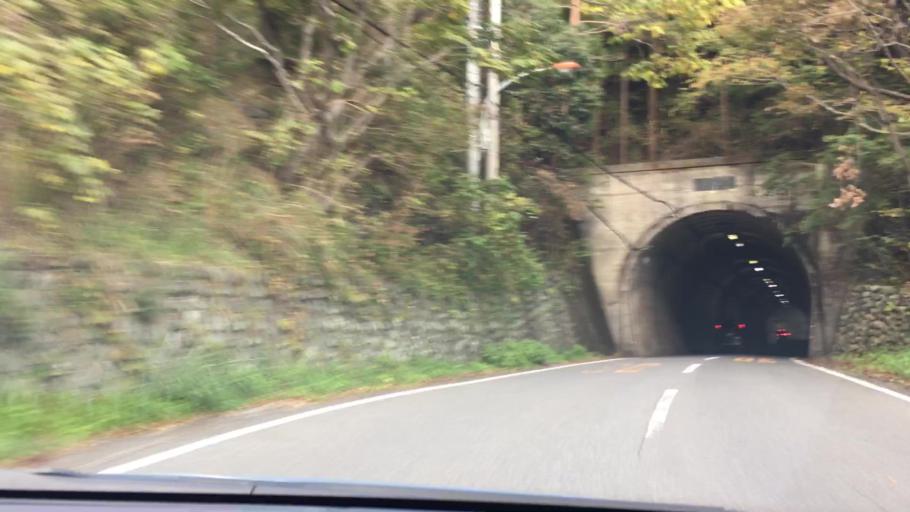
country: JP
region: Yamanashi
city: Uenohara
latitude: 35.5591
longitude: 139.1404
